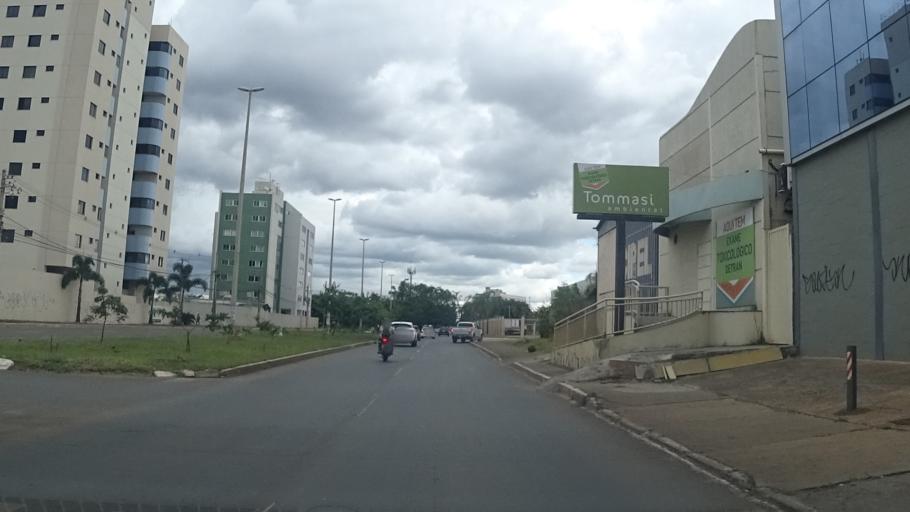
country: BR
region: Federal District
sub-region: Brasilia
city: Brasilia
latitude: -15.8553
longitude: -48.0362
